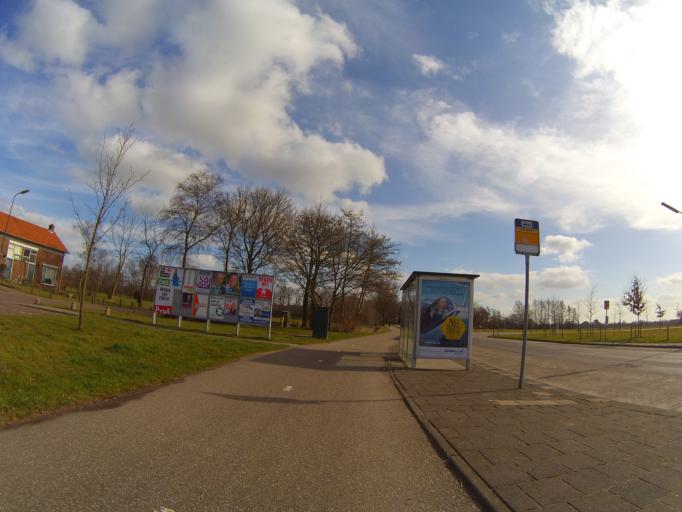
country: NL
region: Utrecht
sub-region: Gemeente Leusden
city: Leusden
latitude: 52.1536
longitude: 5.4338
